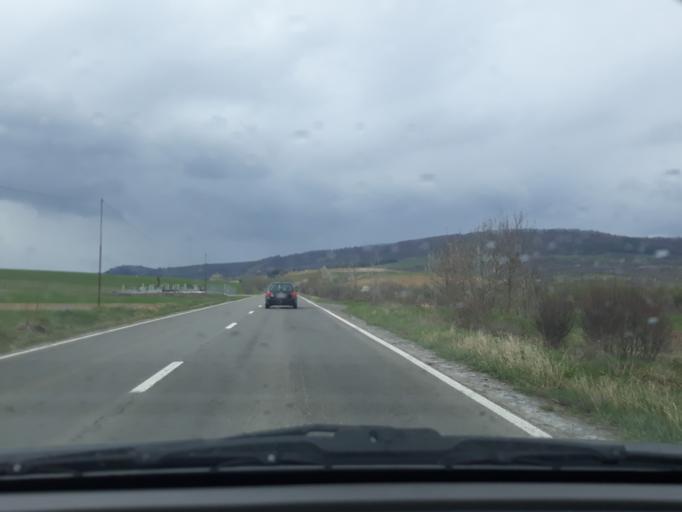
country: RO
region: Harghita
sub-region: Comuna Lupeni
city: Lupeni
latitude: 46.3905
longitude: 25.2155
